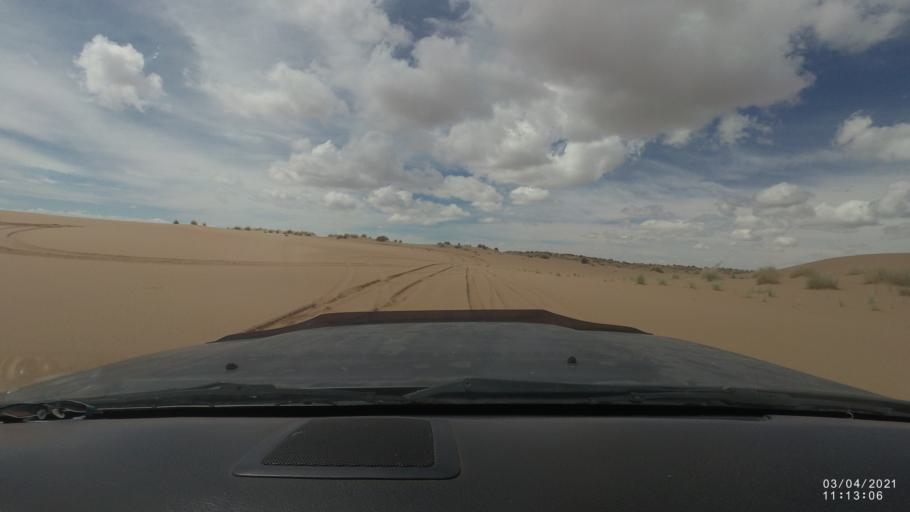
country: BO
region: Oruro
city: Poopo
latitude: -18.7044
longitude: -67.5181
